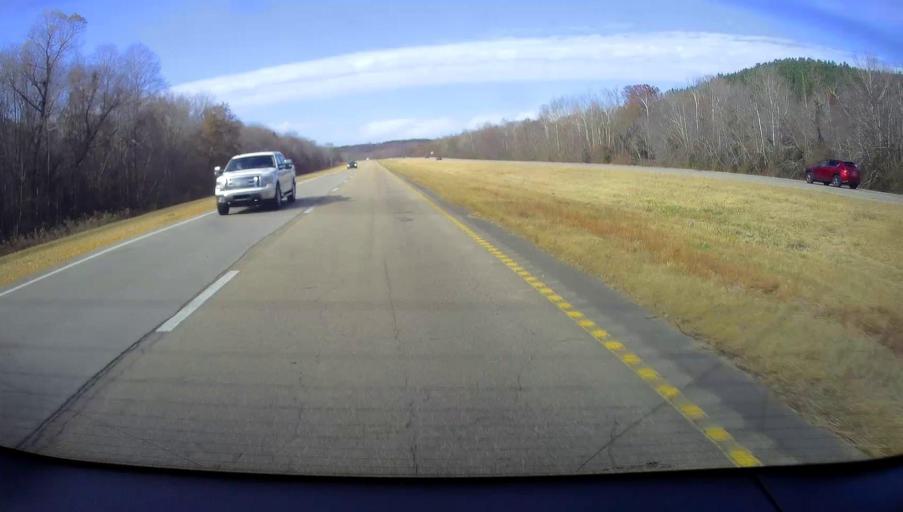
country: US
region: Mississippi
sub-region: Alcorn County
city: Corinth
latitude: 34.9401
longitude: -88.7803
